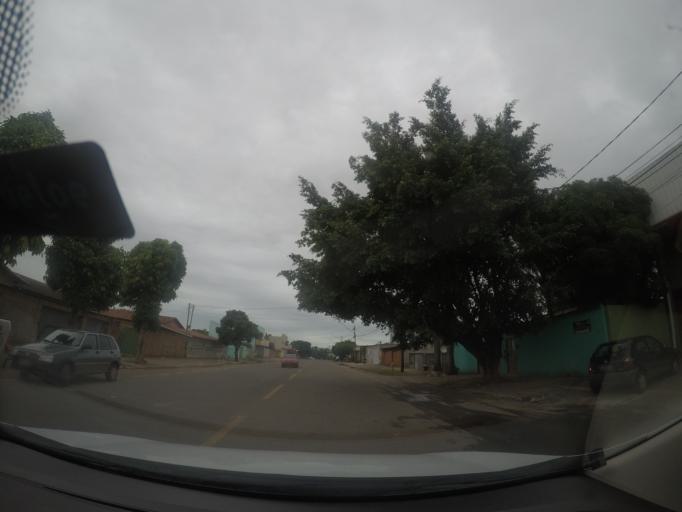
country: BR
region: Goias
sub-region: Goiania
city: Goiania
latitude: -16.6846
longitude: -49.3318
